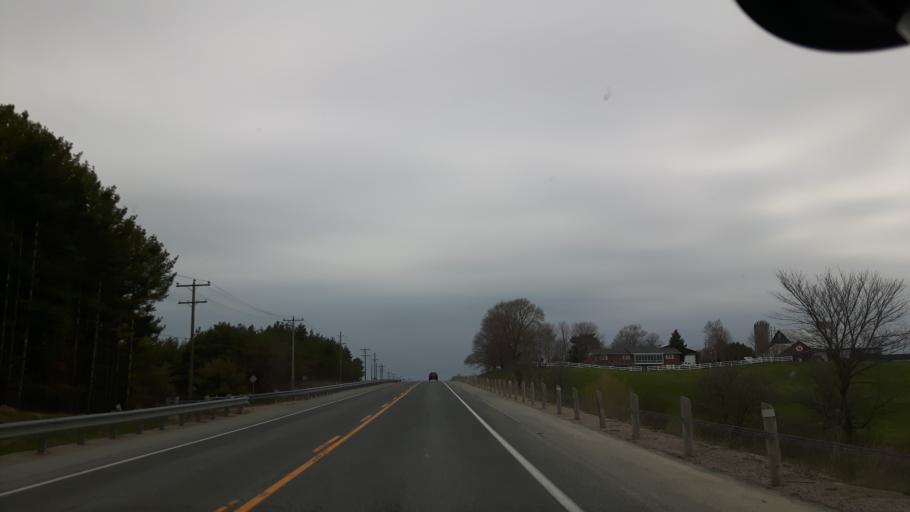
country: CA
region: Ontario
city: Goderich
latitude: 43.6709
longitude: -81.6232
